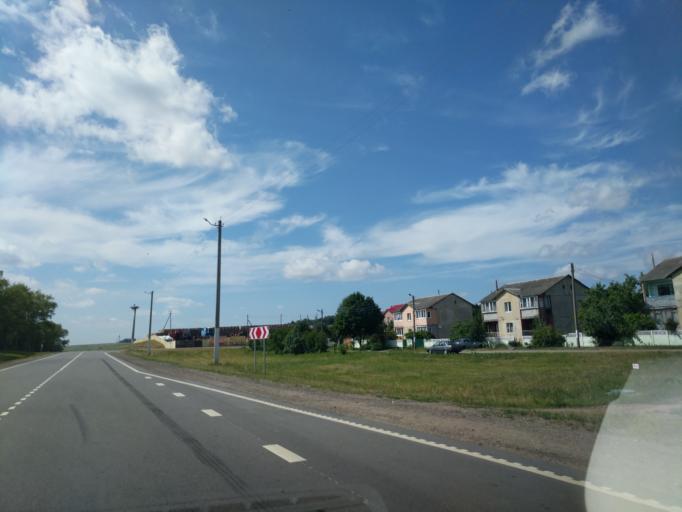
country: BY
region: Minsk
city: Syomkava
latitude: 54.1092
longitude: 27.4582
